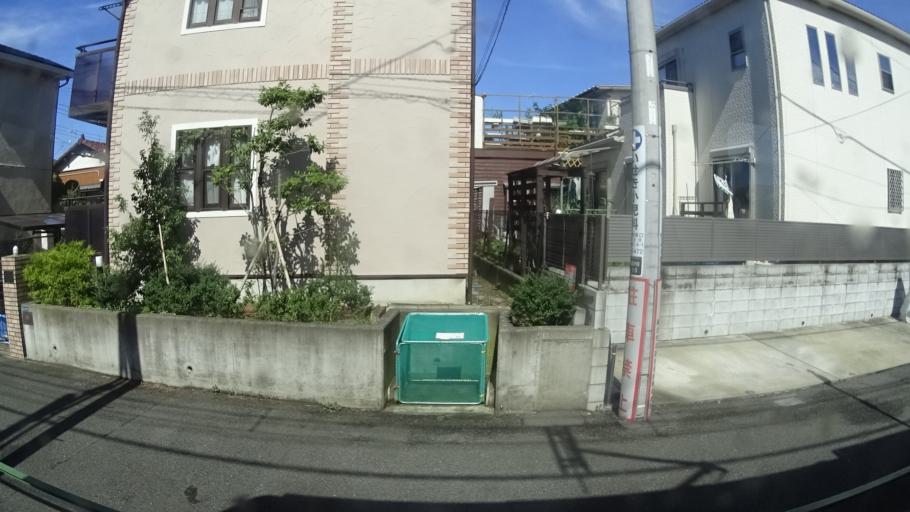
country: JP
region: Kanagawa
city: Fujisawa
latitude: 35.3268
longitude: 139.4851
